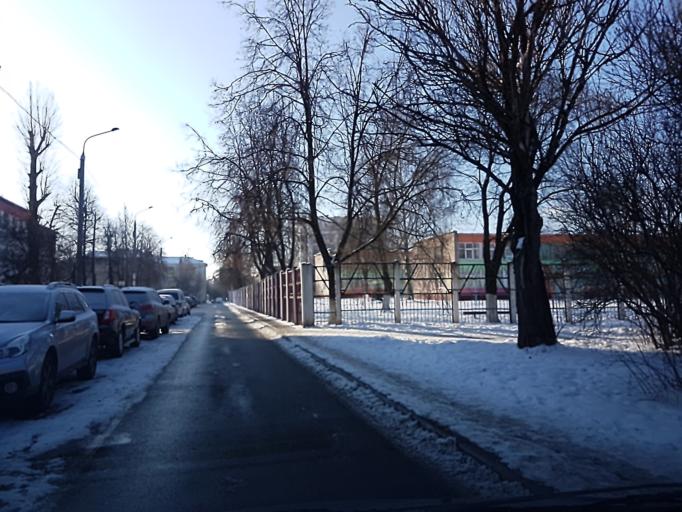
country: BY
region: Minsk
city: Minsk
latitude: 53.9257
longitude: 27.5527
